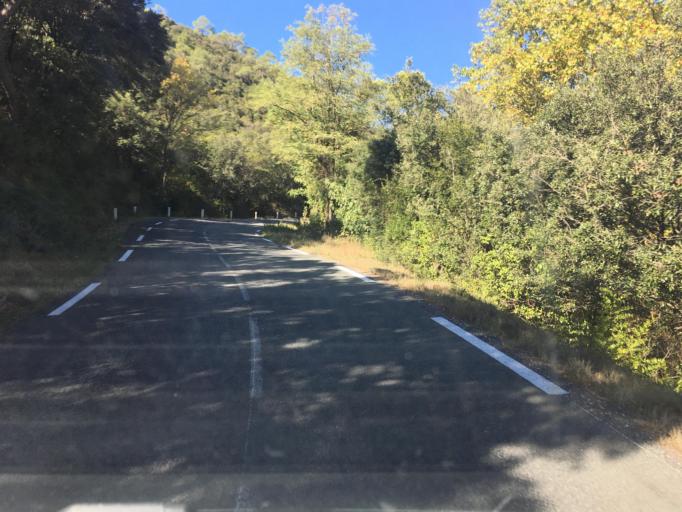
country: FR
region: Languedoc-Roussillon
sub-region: Departement de l'Herault
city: Nebian
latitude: 43.6124
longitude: 3.3803
